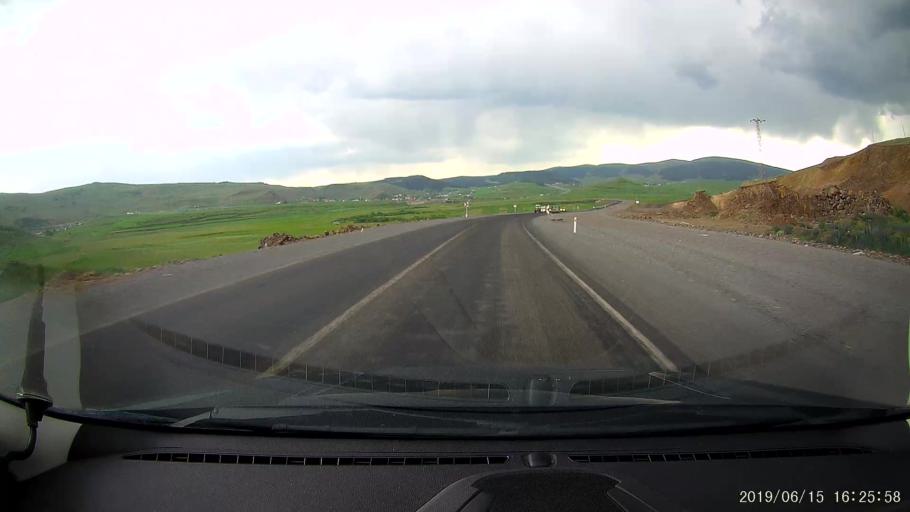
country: TR
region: Ardahan
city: Hanak
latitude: 41.1471
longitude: 42.8655
